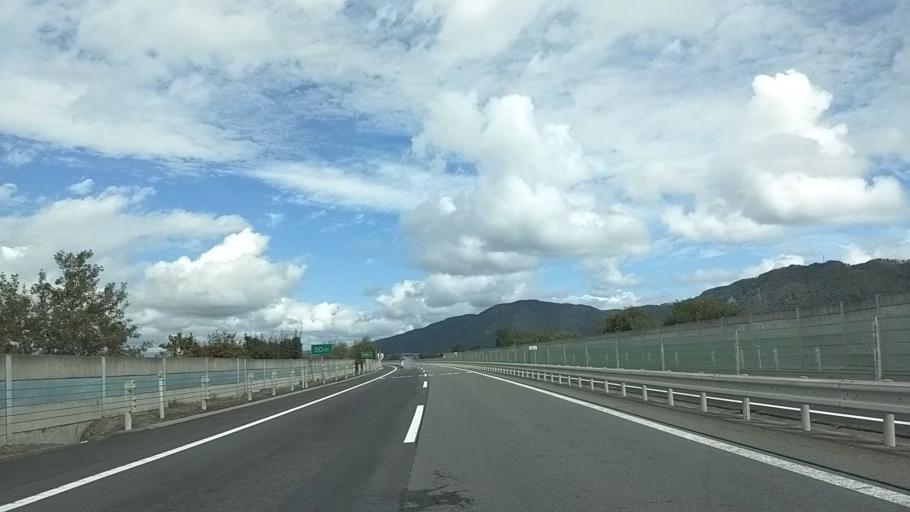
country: JP
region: Nagano
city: Toyoshina
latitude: 36.2770
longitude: 137.9312
